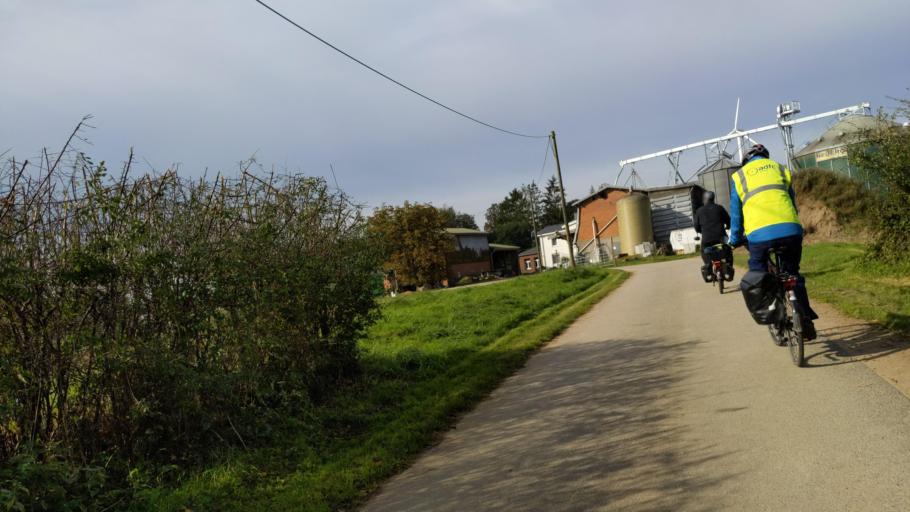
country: DE
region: Schleswig-Holstein
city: Zarpen
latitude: 53.8831
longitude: 10.5010
